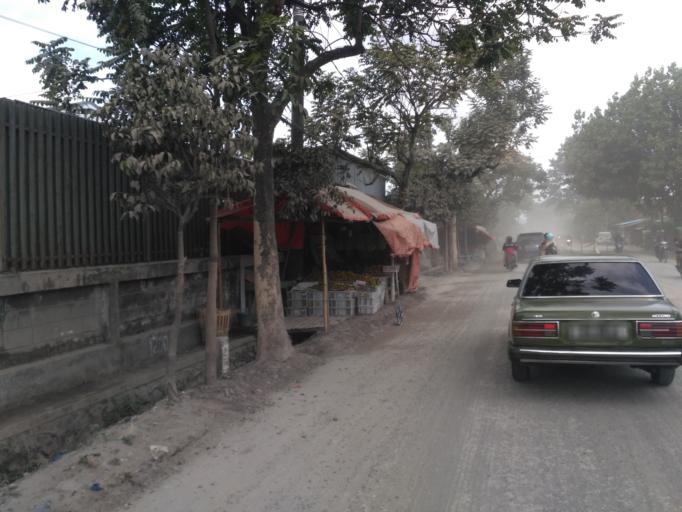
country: ID
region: East Java
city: Kebonsari
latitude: -8.0247
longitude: 112.6276
